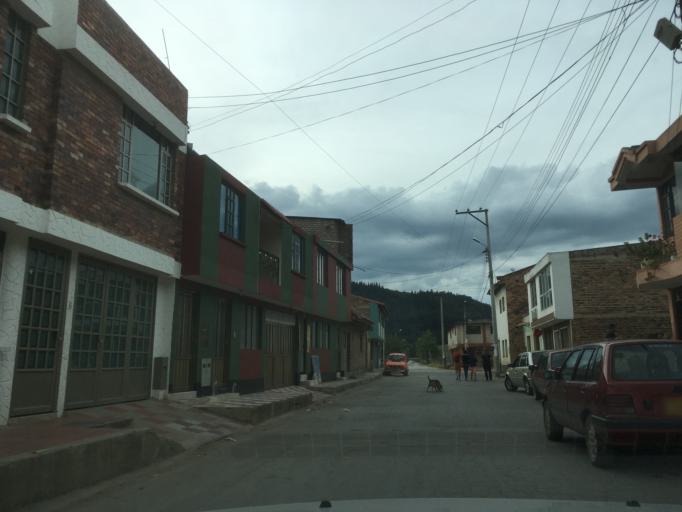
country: CO
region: Boyaca
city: Firavitoba
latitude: 5.6680
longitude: -72.9934
